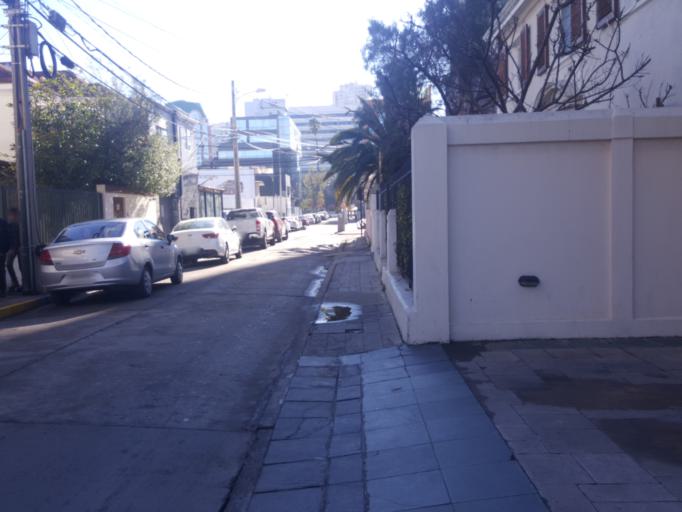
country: CL
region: Valparaiso
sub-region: Provincia de Valparaiso
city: Vina del Mar
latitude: -33.0118
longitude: -71.5485
